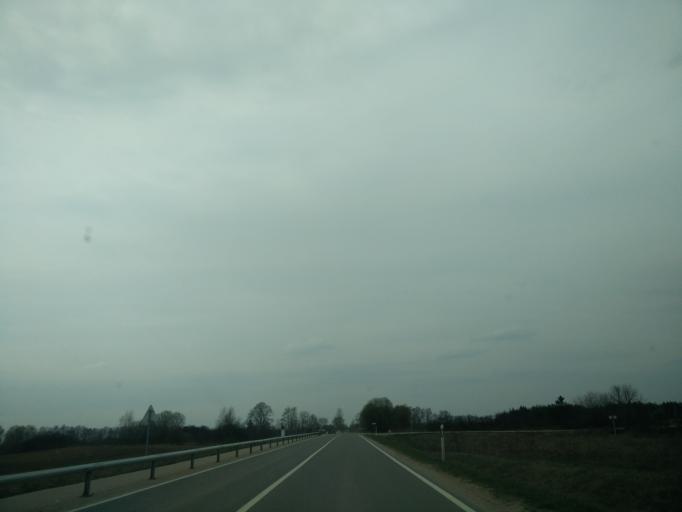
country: LT
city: Trakai
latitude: 54.6156
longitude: 24.9734
